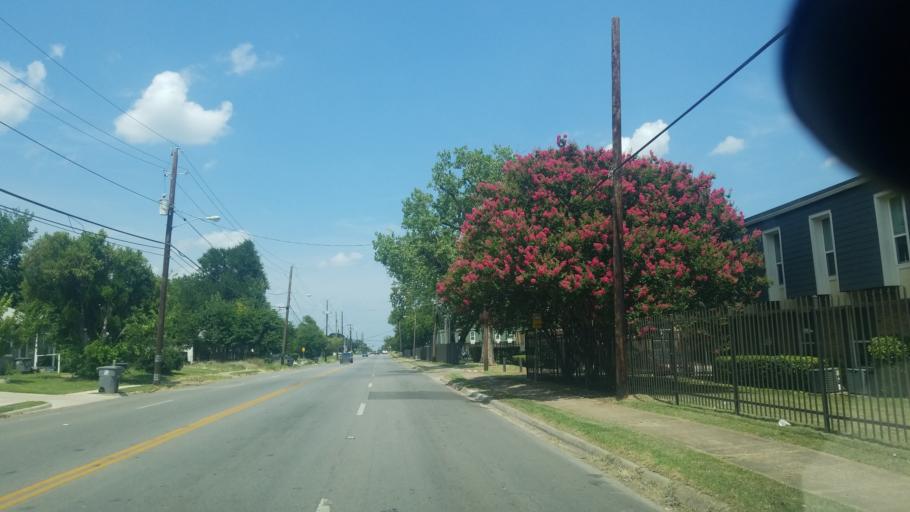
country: US
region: Texas
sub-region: Dallas County
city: Dallas
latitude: 32.7138
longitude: -96.7792
